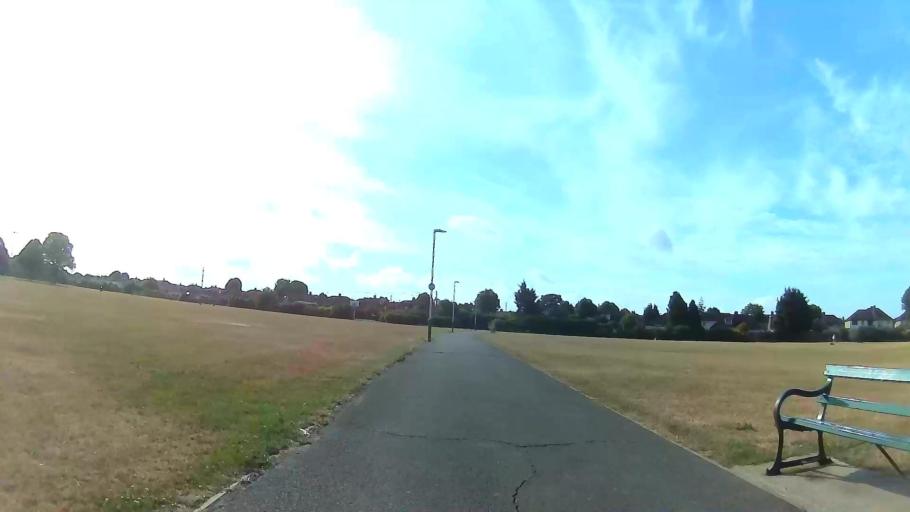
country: GB
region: England
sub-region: Greater London
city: Elm Park
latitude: 51.5548
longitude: 0.1960
